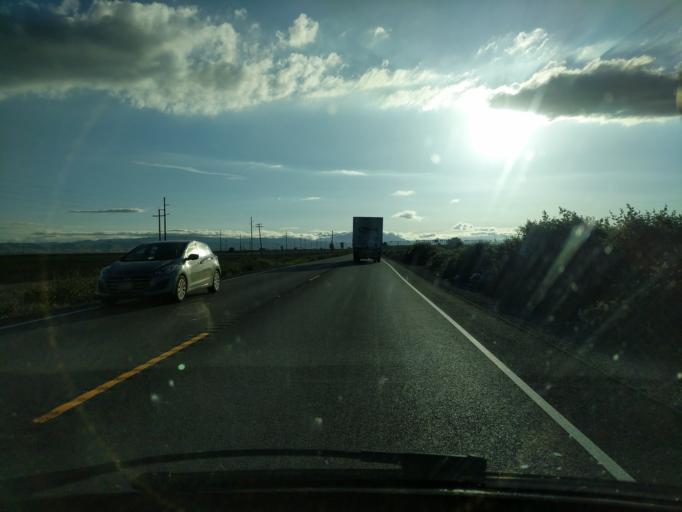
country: US
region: California
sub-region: Contra Costa County
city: Discovery Bay
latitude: 37.8900
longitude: -121.5611
